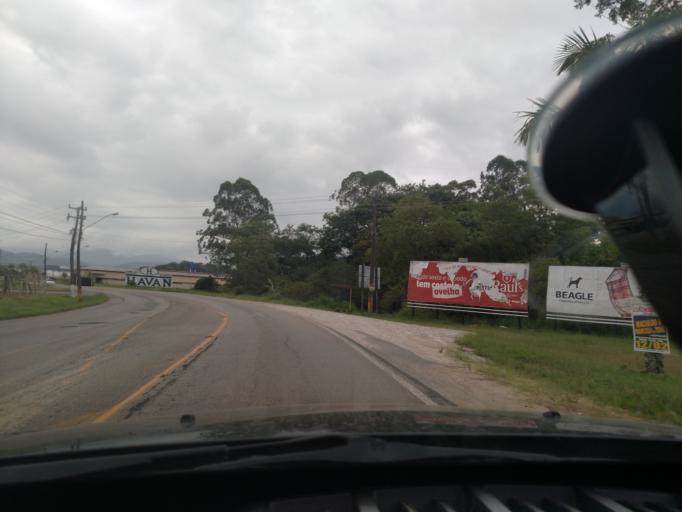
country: BR
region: Santa Catarina
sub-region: Gaspar
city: Gaspar
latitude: -26.9110
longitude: -48.9351
